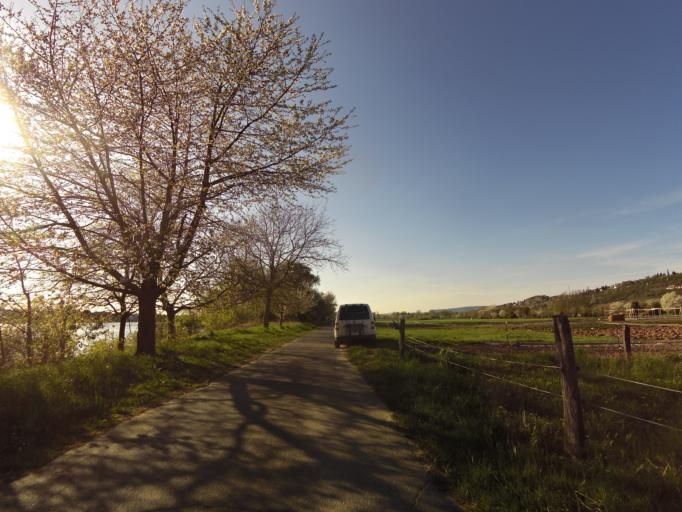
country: DE
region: Rheinland-Pfalz
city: Weitersburg
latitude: 50.3975
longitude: 7.5961
